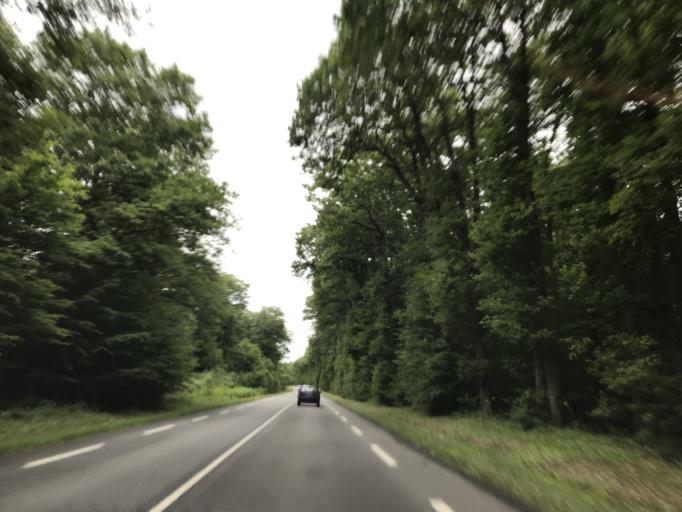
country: FR
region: Haute-Normandie
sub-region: Departement de l'Eure
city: La Couture-Boussey
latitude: 48.9070
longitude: 1.3779
